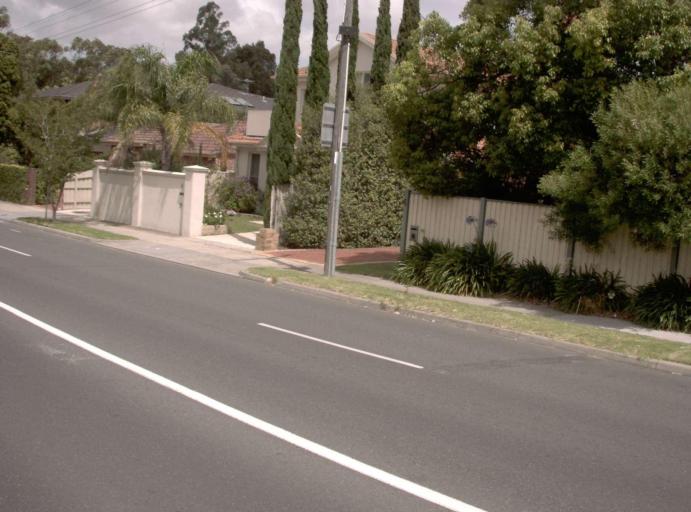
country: AU
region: Victoria
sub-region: Boroondara
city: Kew East
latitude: -37.8009
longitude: 145.0634
